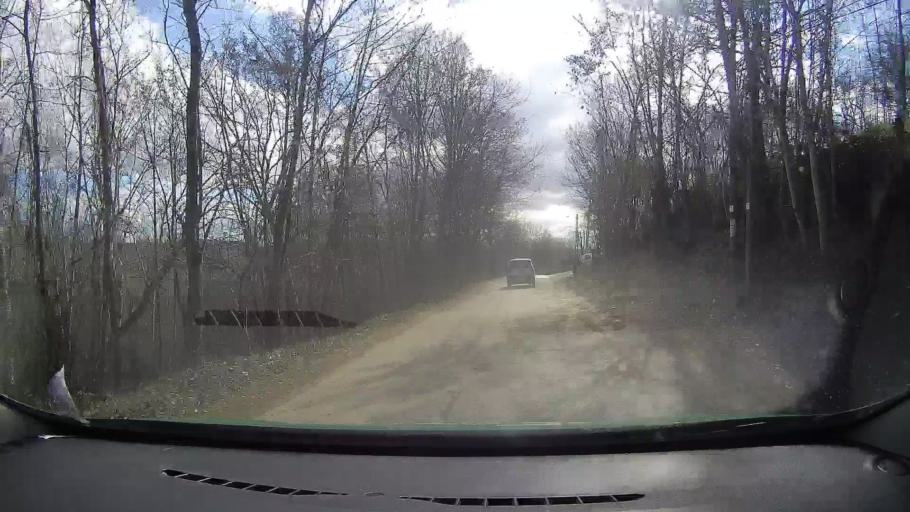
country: RO
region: Dambovita
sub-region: Oras Pucioasa
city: Pucioasa
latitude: 45.0667
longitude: 25.4237
